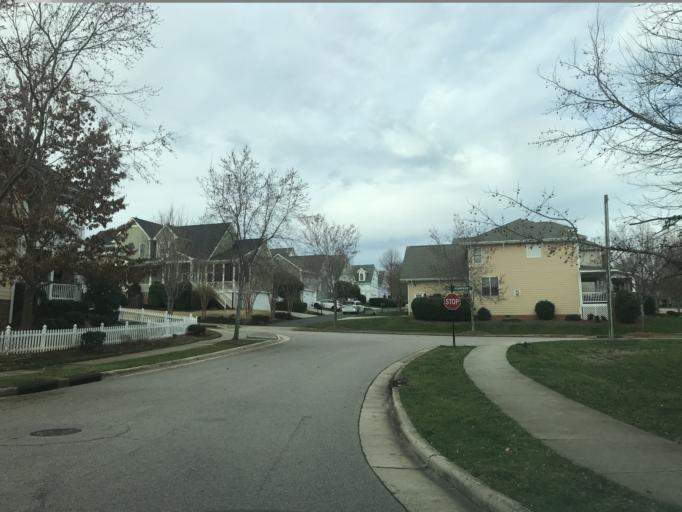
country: US
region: North Carolina
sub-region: Wake County
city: Wake Forest
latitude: 35.9246
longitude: -78.5721
